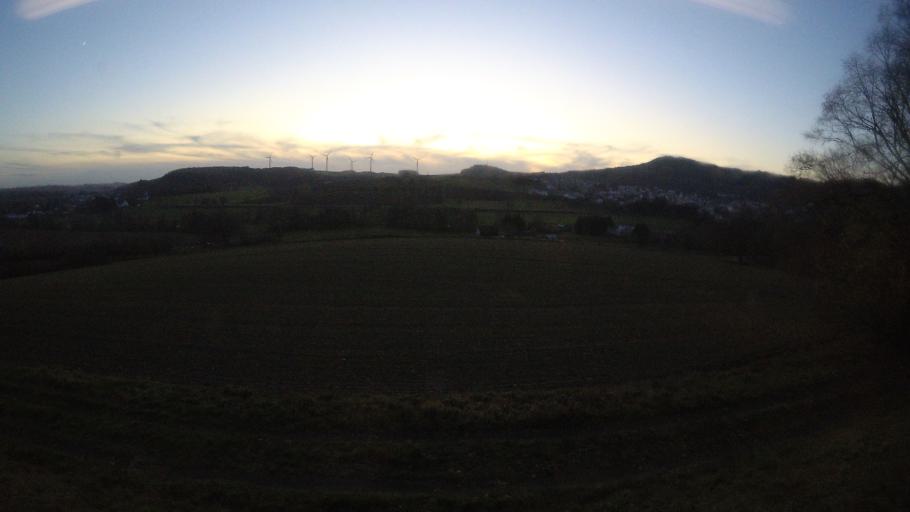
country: DE
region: Rheinland-Pfalz
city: Reichweiler
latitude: 49.5229
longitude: 7.2744
